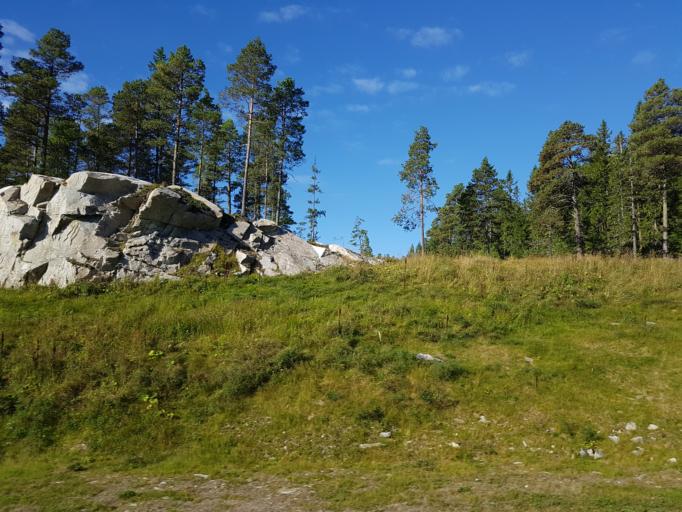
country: NO
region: Sor-Trondelag
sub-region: Trondheim
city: Trondheim
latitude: 63.6102
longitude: 10.2379
